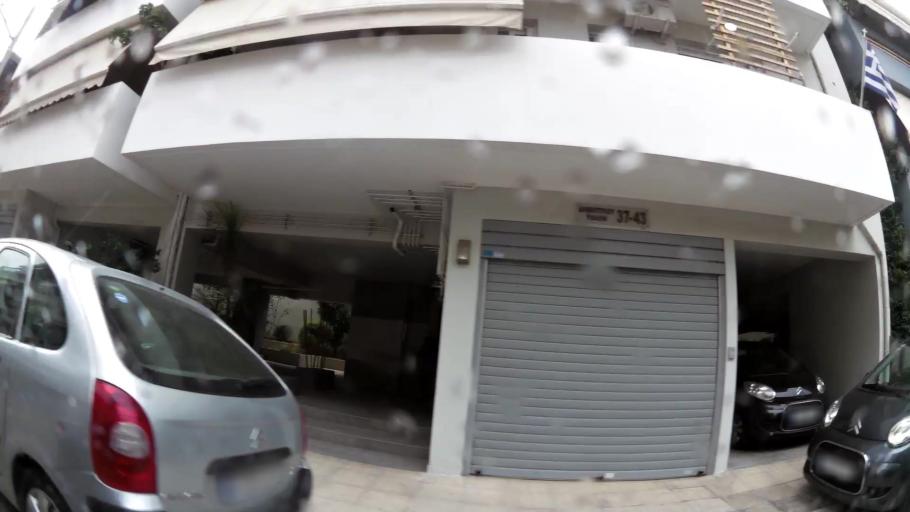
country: GR
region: Attica
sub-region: Nomos Attikis
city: Piraeus
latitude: 37.9359
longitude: 23.6335
